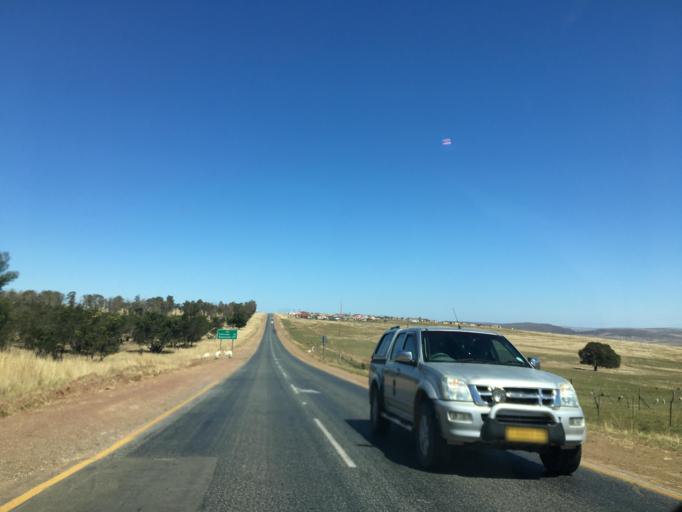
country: ZA
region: Eastern Cape
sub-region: Chris Hani District Municipality
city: Cofimvaba
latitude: -31.9182
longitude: 27.8381
